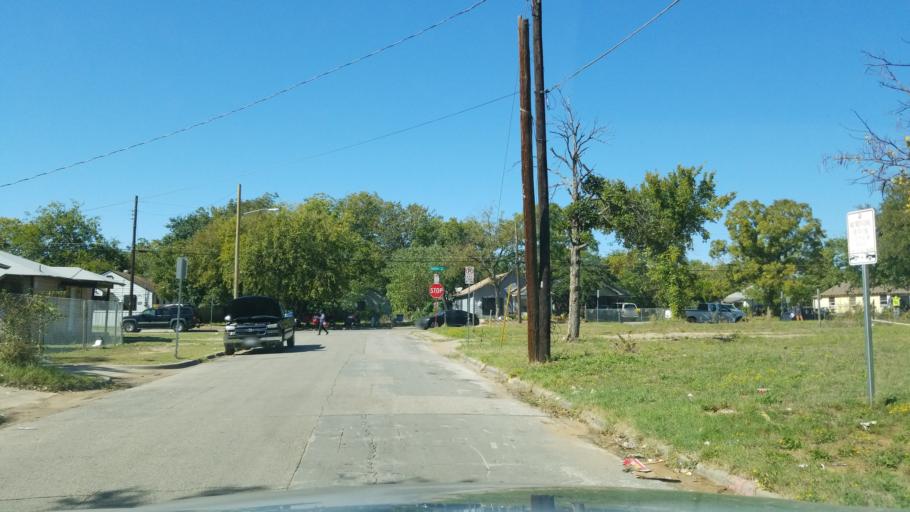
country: US
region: Texas
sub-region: Dallas County
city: Dallas
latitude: 32.7758
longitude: -96.7422
